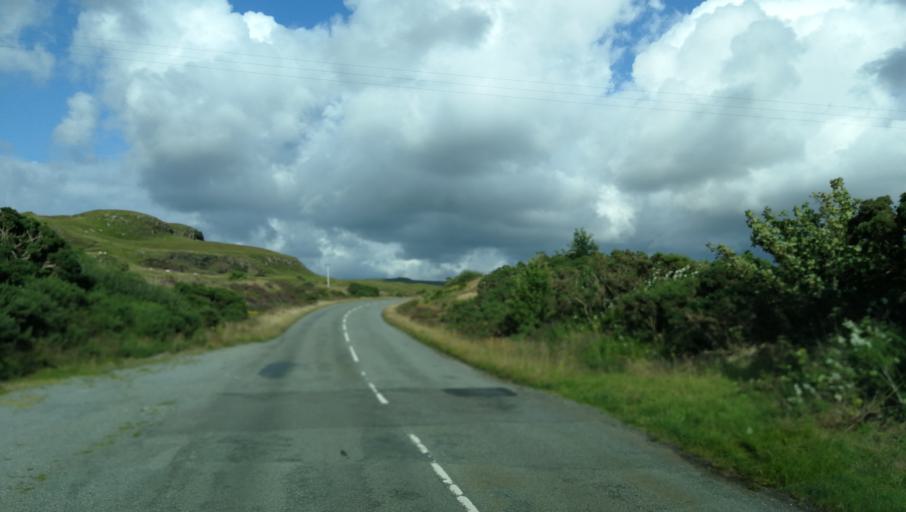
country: GB
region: Scotland
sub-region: Highland
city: Isle of Skye
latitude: 57.4388
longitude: -6.5635
